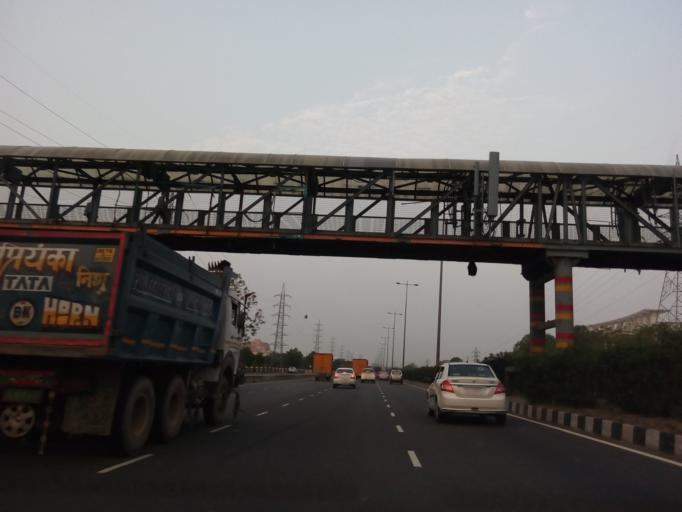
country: IN
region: Haryana
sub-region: Gurgaon
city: Gurgaon
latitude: 28.4912
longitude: 77.0821
